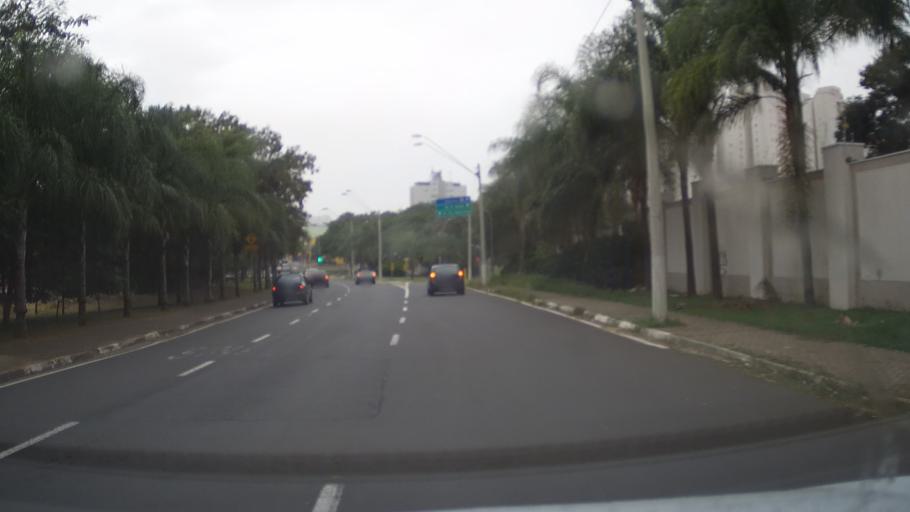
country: BR
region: Sao Paulo
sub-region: Campinas
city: Campinas
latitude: -22.9295
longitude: -47.0585
